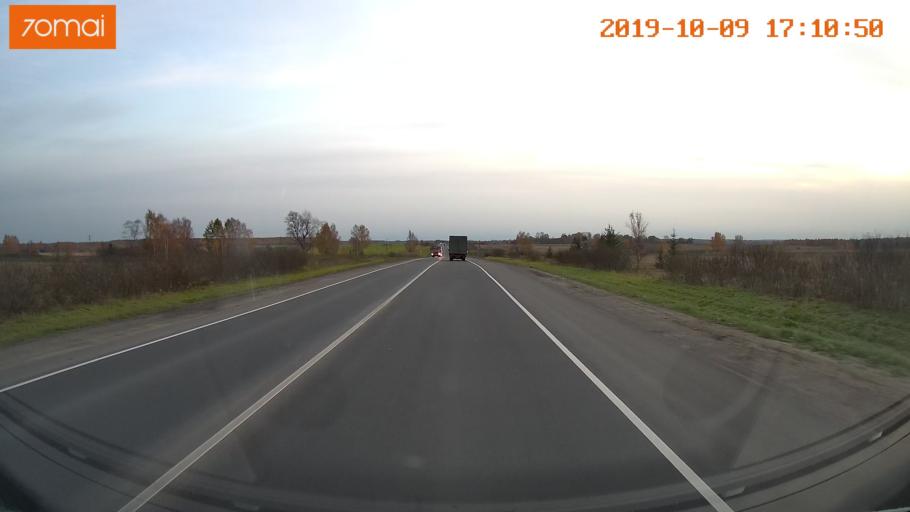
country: RU
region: Ivanovo
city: Privolzhsk
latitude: 57.3505
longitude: 41.2544
